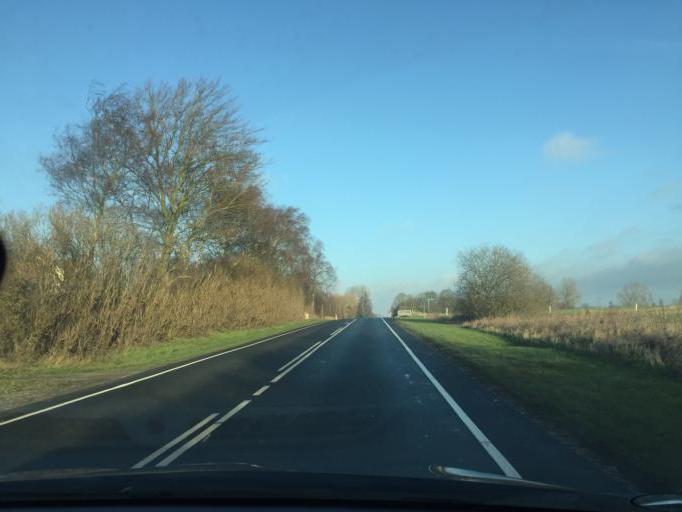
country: DK
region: South Denmark
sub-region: Faaborg-Midtfyn Kommune
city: Faaborg
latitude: 55.1781
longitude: 10.2946
